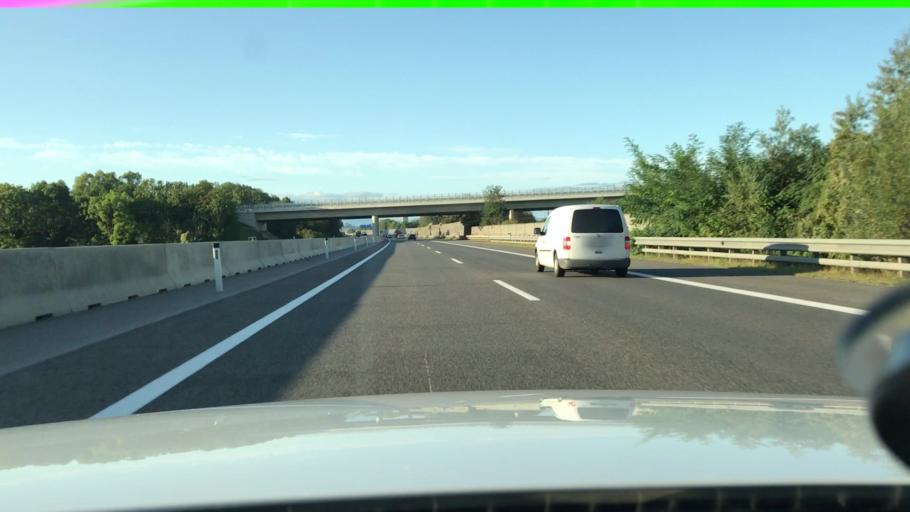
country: AT
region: Lower Austria
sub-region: Politischer Bezirk Sankt Polten
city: Herzogenburg
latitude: 48.2953
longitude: 15.7043
